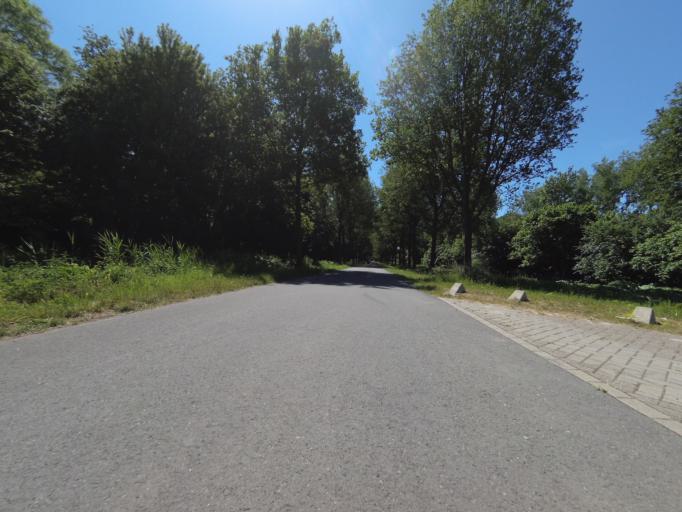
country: NL
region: Flevoland
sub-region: Gemeente Zeewolde
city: Zeewolde
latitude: 52.3292
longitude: 5.4979
